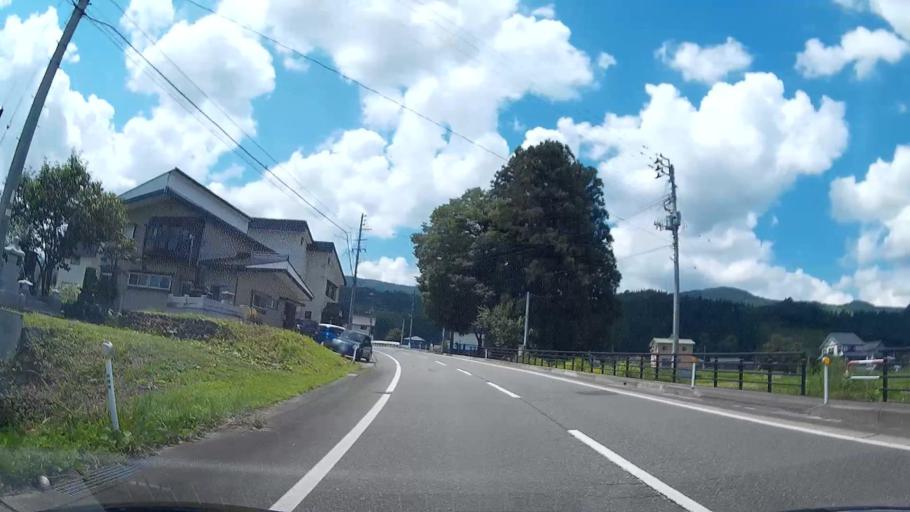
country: JP
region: Niigata
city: Shiozawa
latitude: 37.0180
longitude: 138.8241
